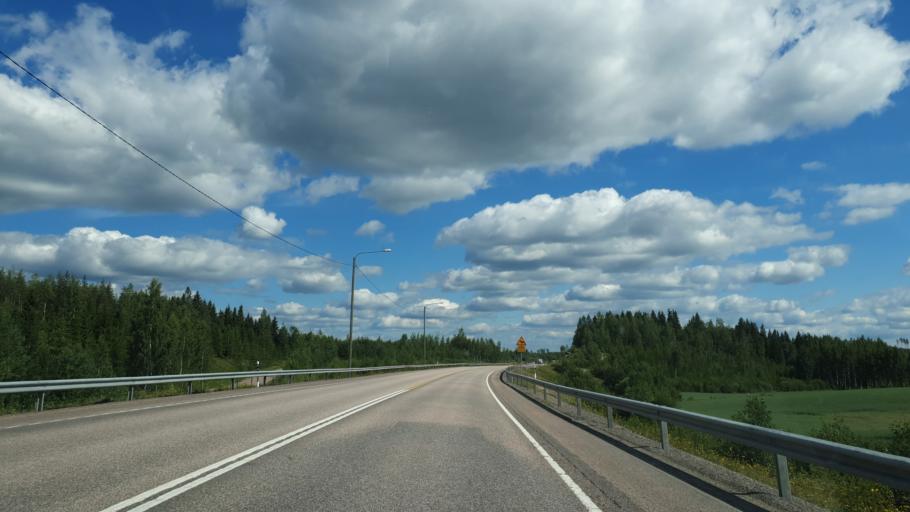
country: FI
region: Pirkanmaa
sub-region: Tampere
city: Kuhmalahti
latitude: 61.7077
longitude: 24.5703
